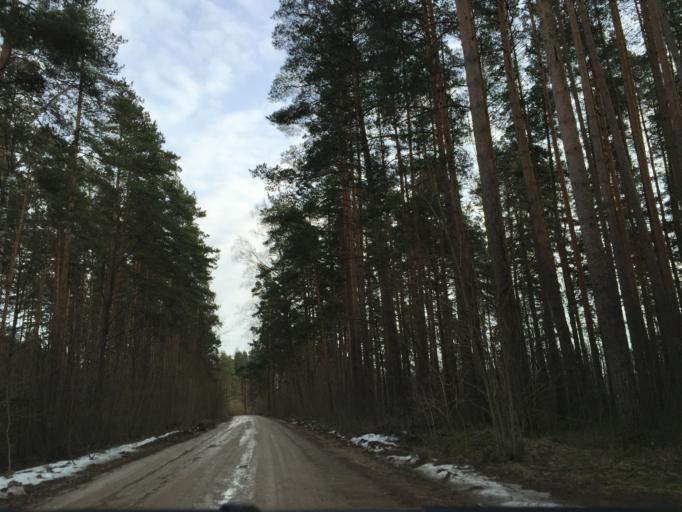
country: LV
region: Stopini
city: Ulbroka
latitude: 56.9232
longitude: 24.2878
